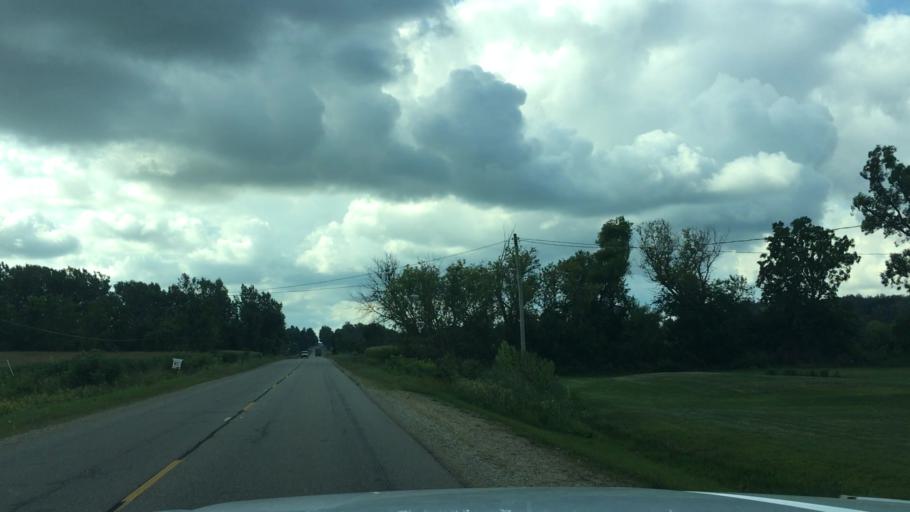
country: US
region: Michigan
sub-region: Ottawa County
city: Hudsonville
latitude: 42.7905
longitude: -85.8418
